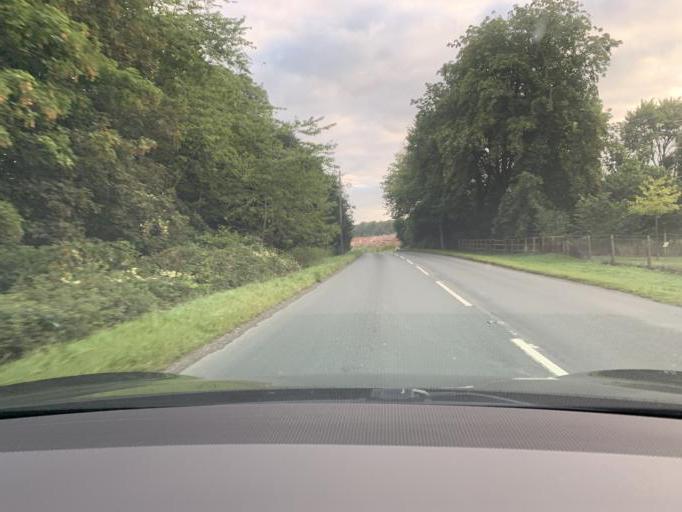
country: GB
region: England
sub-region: Wiltshire
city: Tidworth
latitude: 51.2238
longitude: -1.6645
